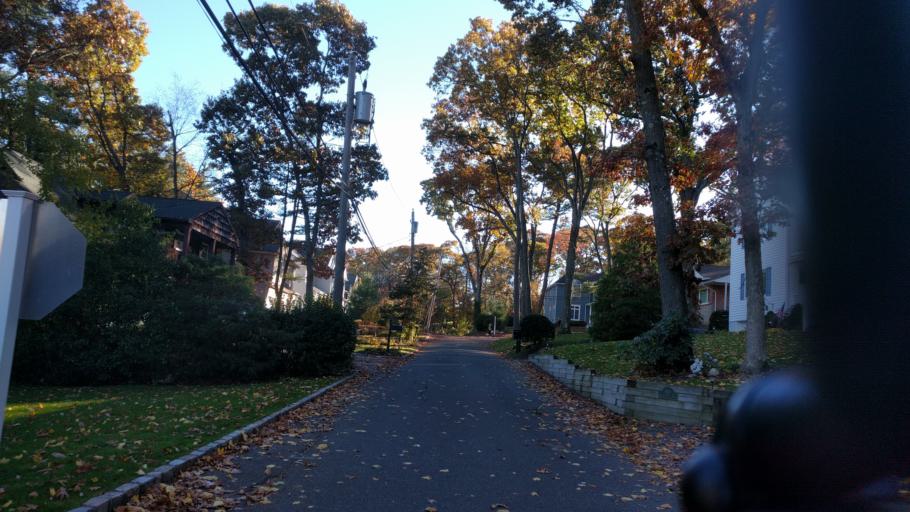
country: US
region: New York
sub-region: Nassau County
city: Bayville
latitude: 40.9000
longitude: -73.5517
